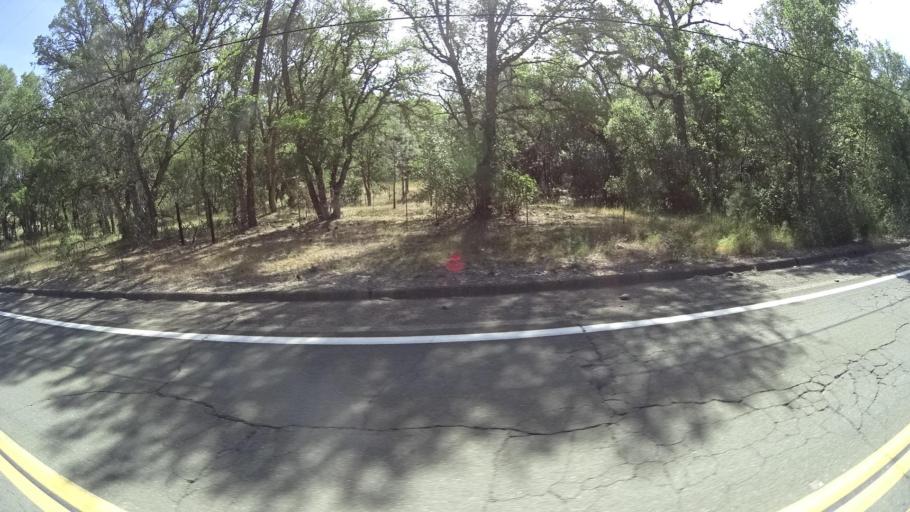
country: US
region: California
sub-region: Lake County
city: Kelseyville
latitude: 38.9432
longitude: -122.8155
